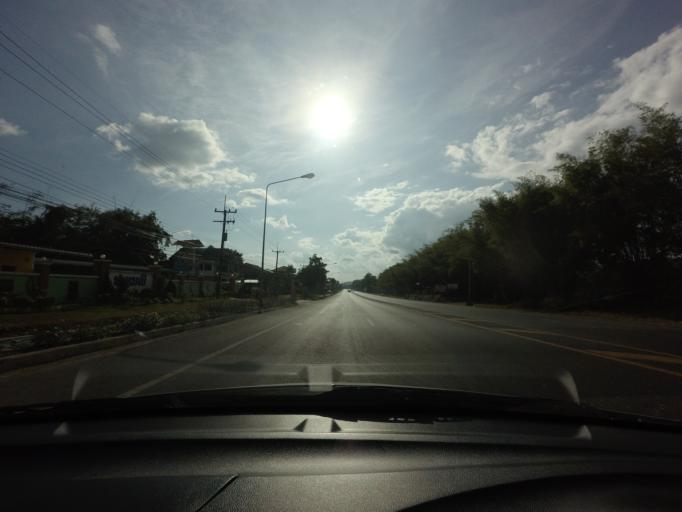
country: TH
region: Nakhon Nayok
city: Nakhon Nayok
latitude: 14.2951
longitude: 101.2911
